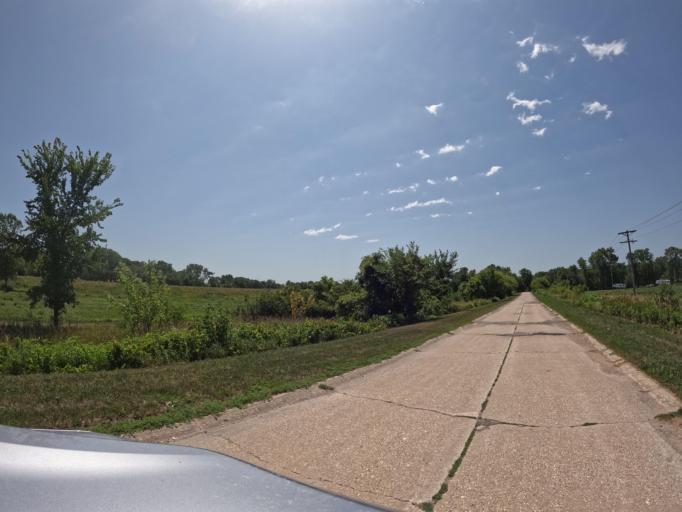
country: US
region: Iowa
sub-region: Henry County
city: Mount Pleasant
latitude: 40.9004
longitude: -91.5562
